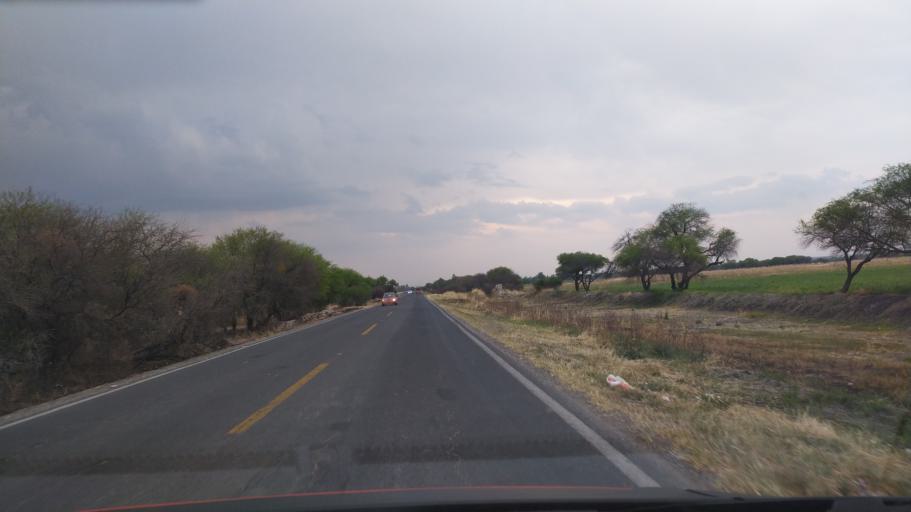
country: MX
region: Guanajuato
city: Ciudad Manuel Doblado
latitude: 20.7726
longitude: -101.9124
